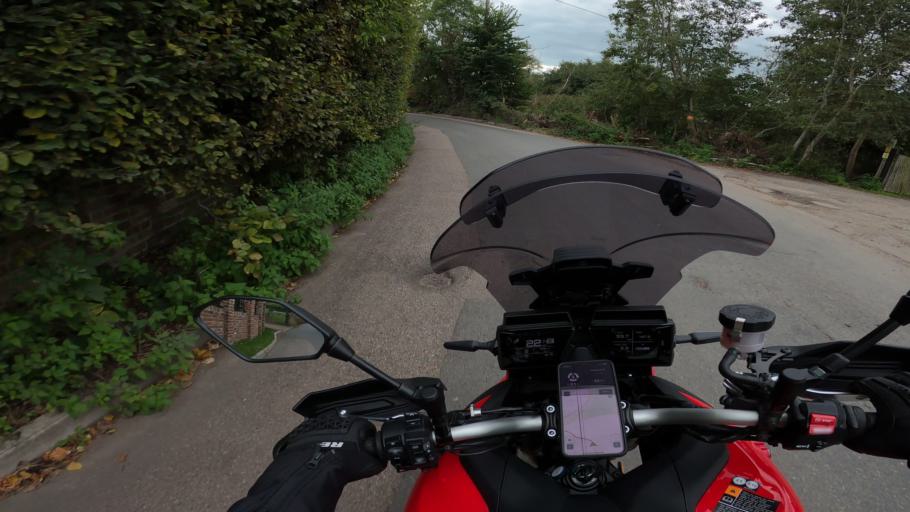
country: GB
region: England
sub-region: Kent
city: Halstead
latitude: 51.3492
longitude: 0.1364
